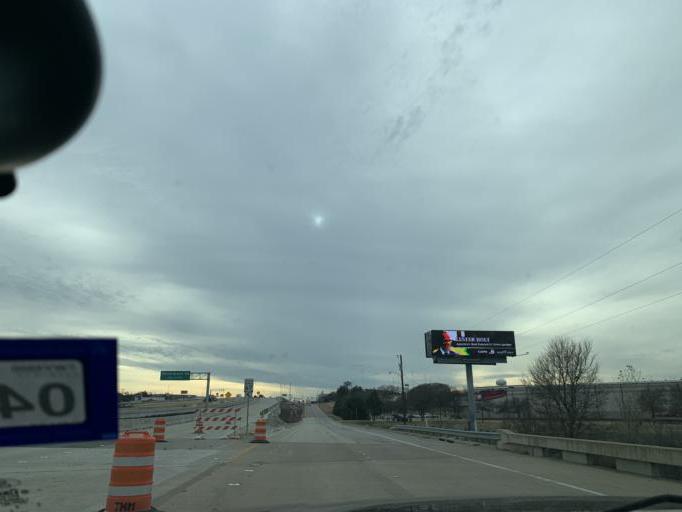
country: US
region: Texas
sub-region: Dallas County
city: Duncanville
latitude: 32.6288
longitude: -96.9051
